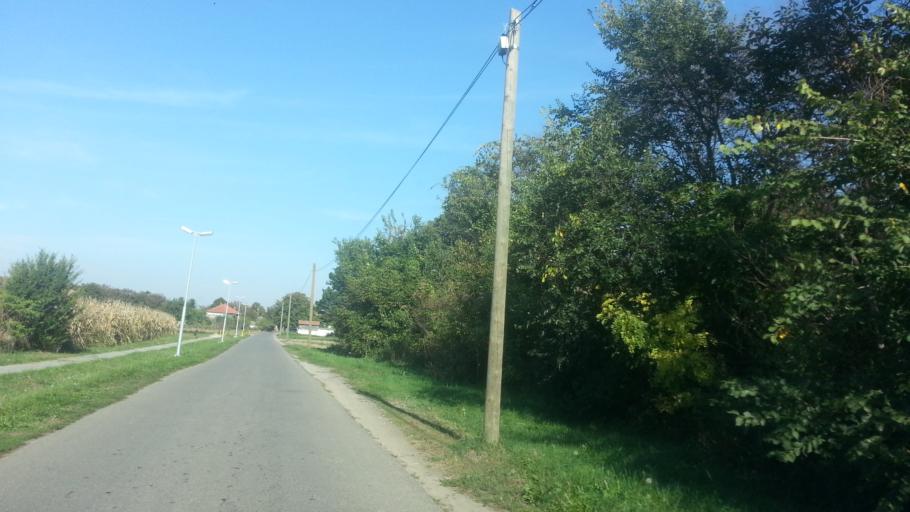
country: RS
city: Belegis
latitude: 45.0213
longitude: 20.3323
